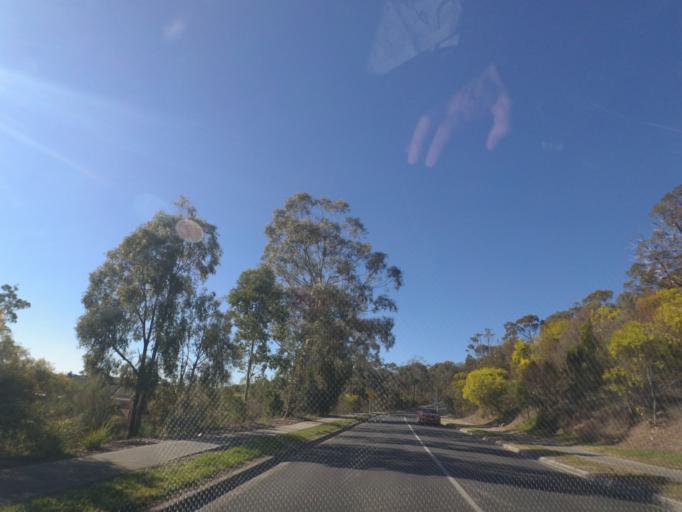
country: AU
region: Victoria
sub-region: Maroondah
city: Croydon Hills
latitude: -37.7702
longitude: 145.2826
